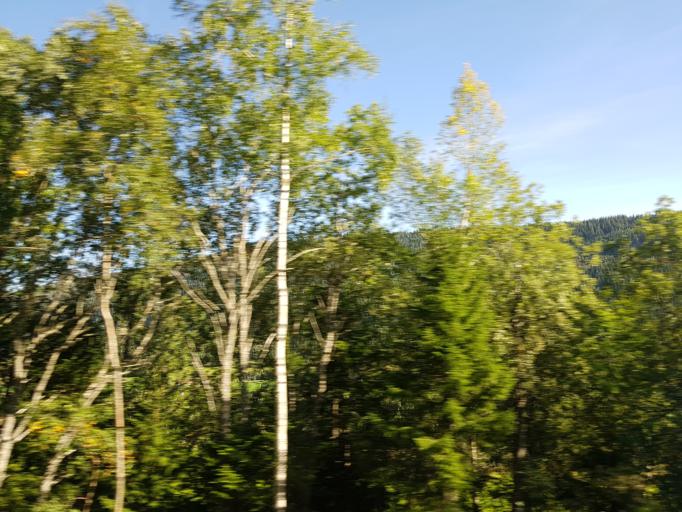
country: NO
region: Sor-Trondelag
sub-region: Afjord
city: A i Afjord
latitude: 63.6869
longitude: 10.2434
